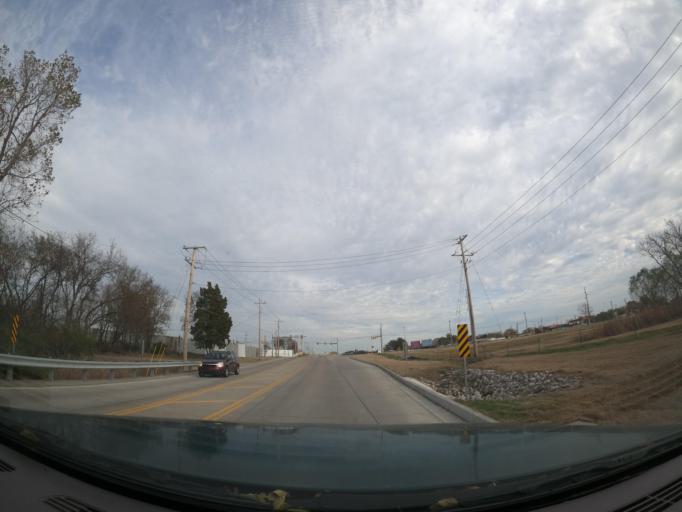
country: US
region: Oklahoma
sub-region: Tulsa County
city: Turley
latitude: 36.2062
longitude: -95.9597
